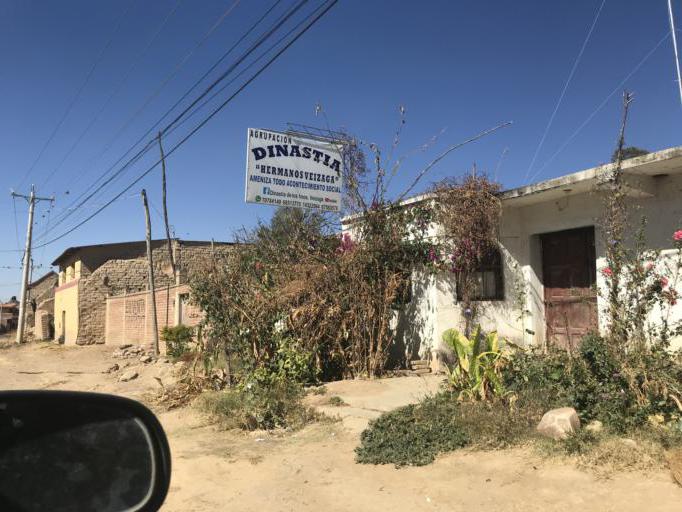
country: BO
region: Cochabamba
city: Tarata
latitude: -17.6028
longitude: -65.9844
